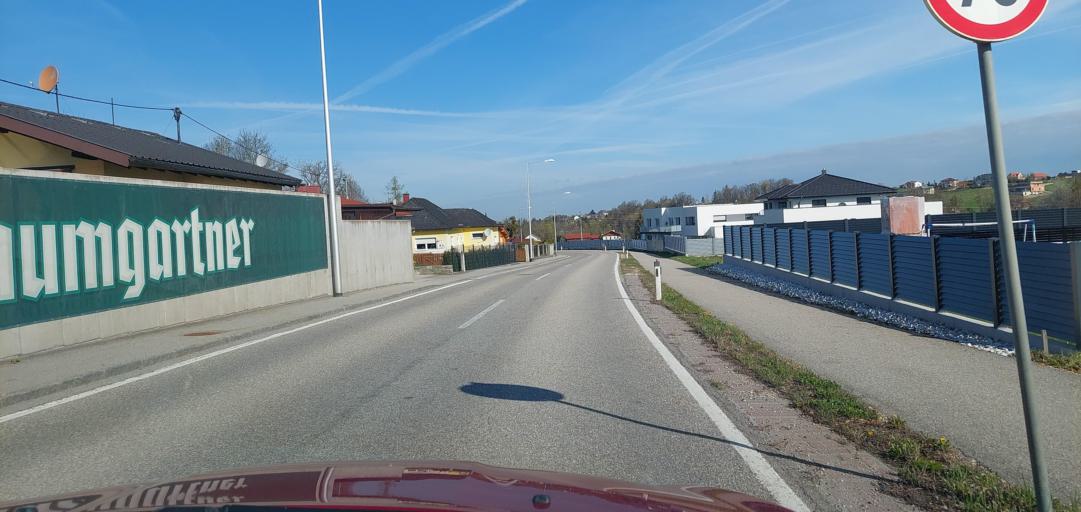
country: AT
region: Upper Austria
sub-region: Politischer Bezirk Ried im Innkreis
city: Ried im Innkreis
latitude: 48.1933
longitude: 13.5050
